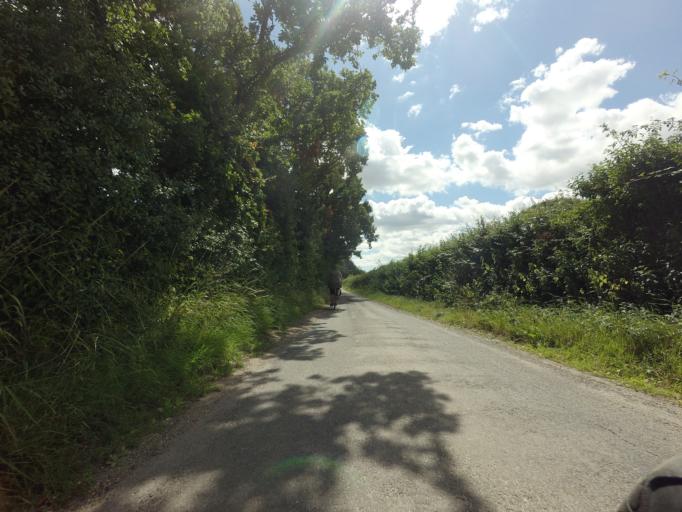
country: GB
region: England
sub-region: East Sussex
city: Ringmer
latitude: 50.8633
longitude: 0.1426
